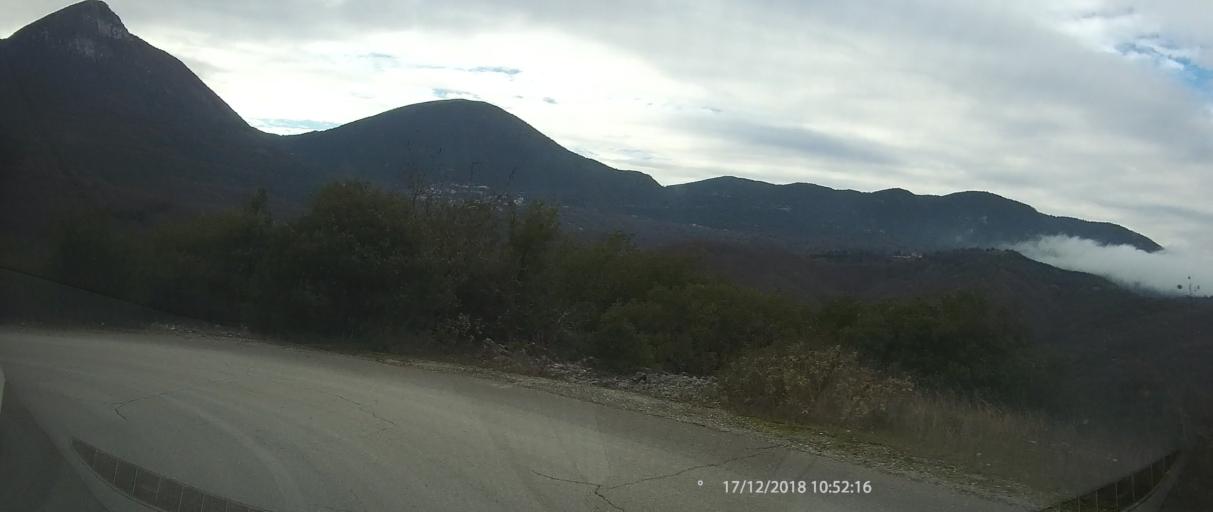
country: GR
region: Epirus
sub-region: Nomos Ioanninon
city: Kalpaki
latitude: 39.9496
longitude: 20.6894
